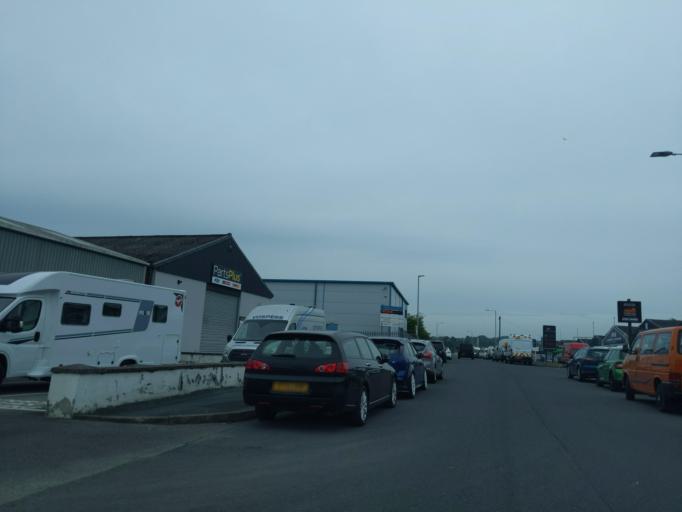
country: GB
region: England
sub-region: Devon
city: Plympton
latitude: 50.3885
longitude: -4.0709
